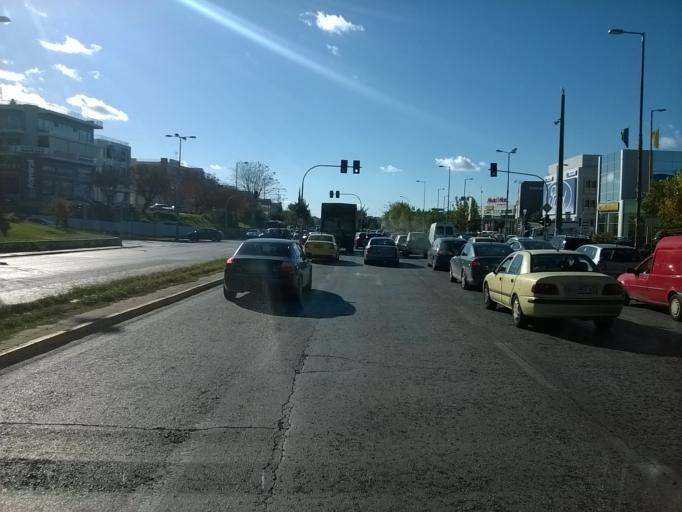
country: GR
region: Attica
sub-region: Nomarchia Athinas
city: Argyroupoli
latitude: 37.9157
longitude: 23.7443
